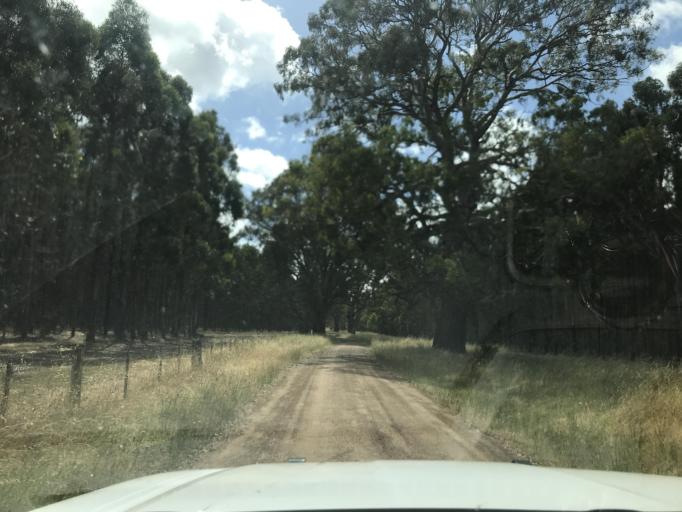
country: AU
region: South Australia
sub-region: Wattle Range
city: Penola
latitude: -37.1898
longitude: 141.3779
